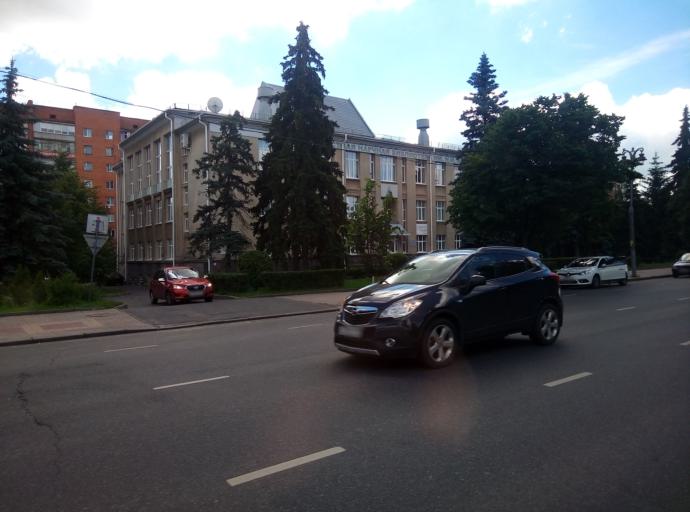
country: RU
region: Kursk
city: Kursk
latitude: 51.7403
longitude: 36.1938
